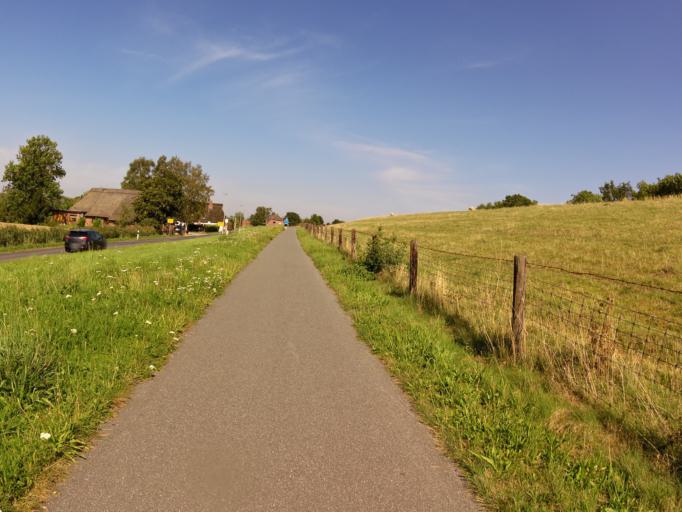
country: DE
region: Lower Saxony
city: Brake (Unterweser)
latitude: 53.2862
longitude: 8.4817
